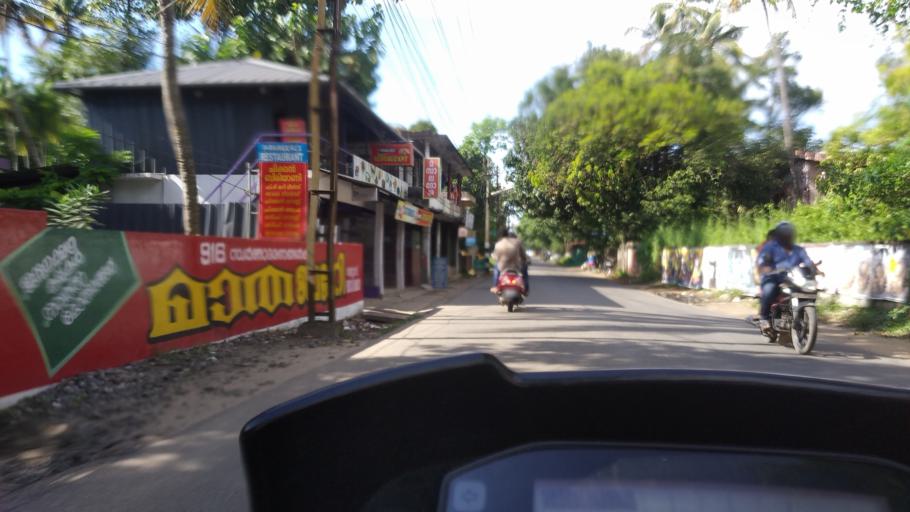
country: IN
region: Kerala
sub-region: Ernakulam
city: Elur
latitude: 10.0677
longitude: 76.2126
